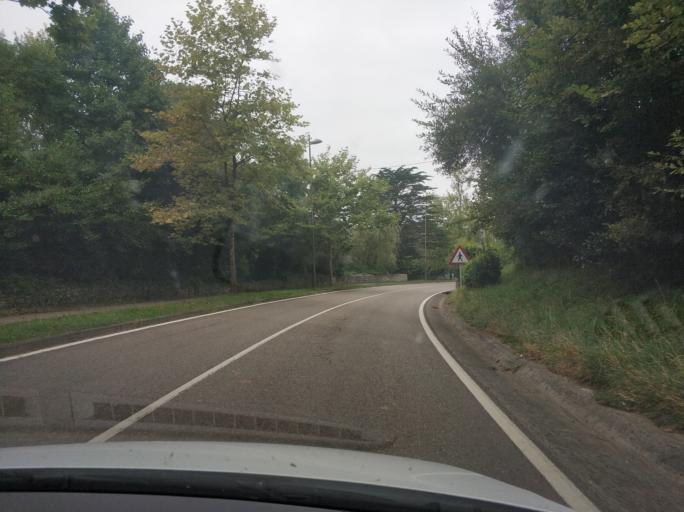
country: ES
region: Cantabria
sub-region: Provincia de Cantabria
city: Comillas
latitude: 43.3790
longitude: -4.3160
